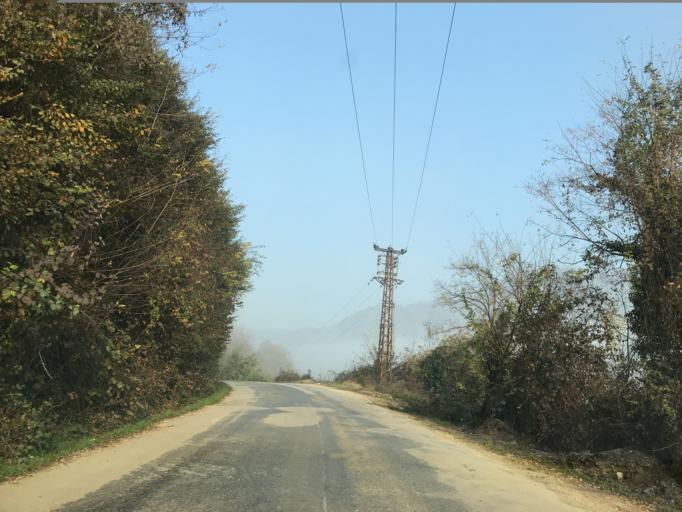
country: TR
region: Duzce
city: Cumayeri
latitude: 40.9100
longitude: 30.9457
